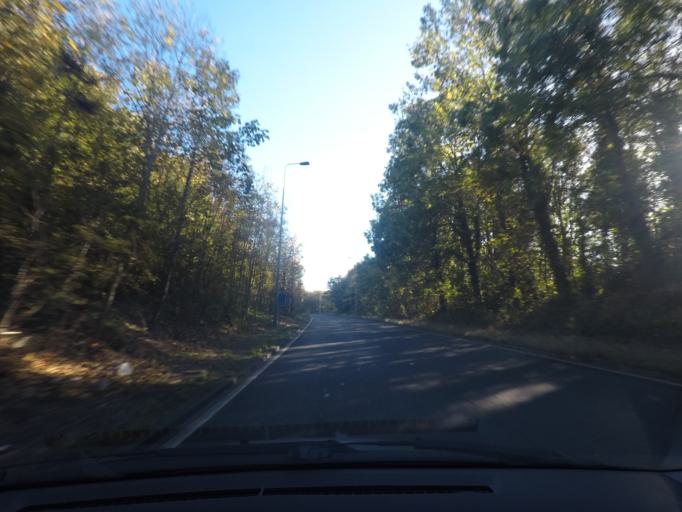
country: GB
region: England
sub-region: East Riding of Yorkshire
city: Hessle
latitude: 53.7215
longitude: -0.4693
